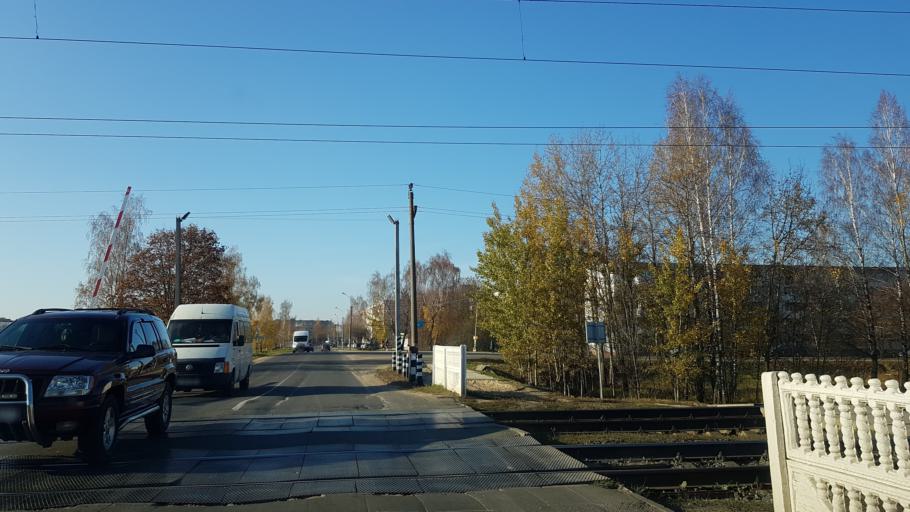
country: BY
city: Fanipol
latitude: 53.7373
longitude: 27.3211
